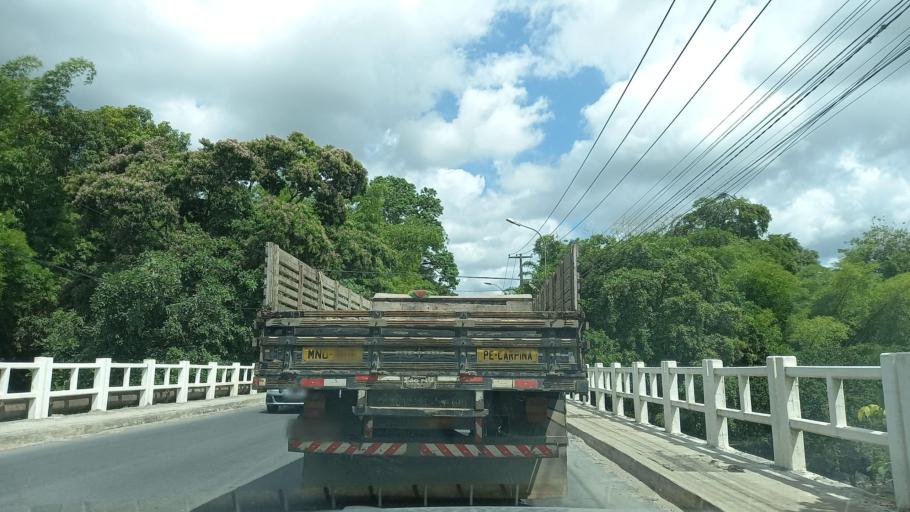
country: BR
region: Pernambuco
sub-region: Jaboatao Dos Guararapes
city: Jaboatao dos Guararapes
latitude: -8.1138
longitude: -35.0072
